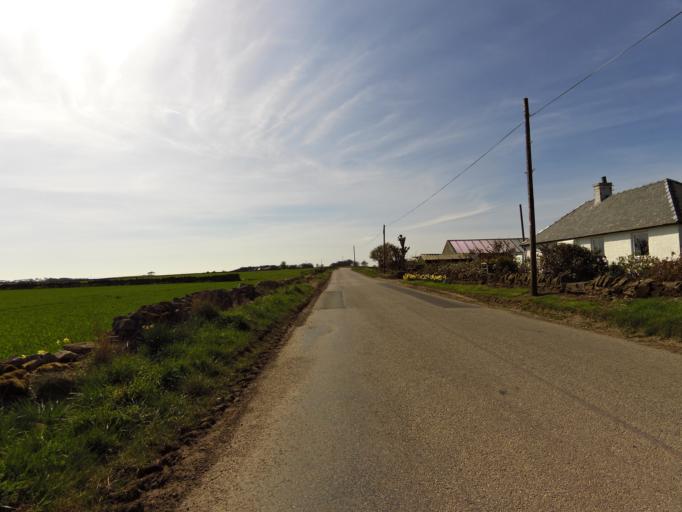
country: GB
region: Scotland
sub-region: Angus
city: Arbroath
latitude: 56.5985
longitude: -2.5454
